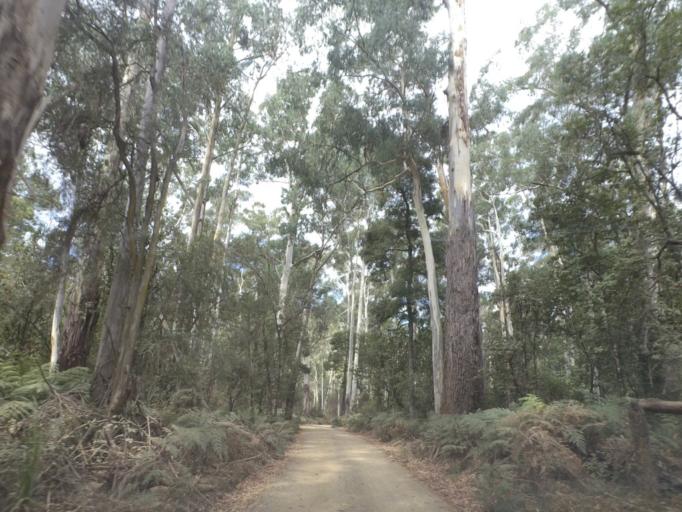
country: AU
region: Victoria
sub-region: Murrindindi
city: Alexandra
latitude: -37.3600
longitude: 145.7534
